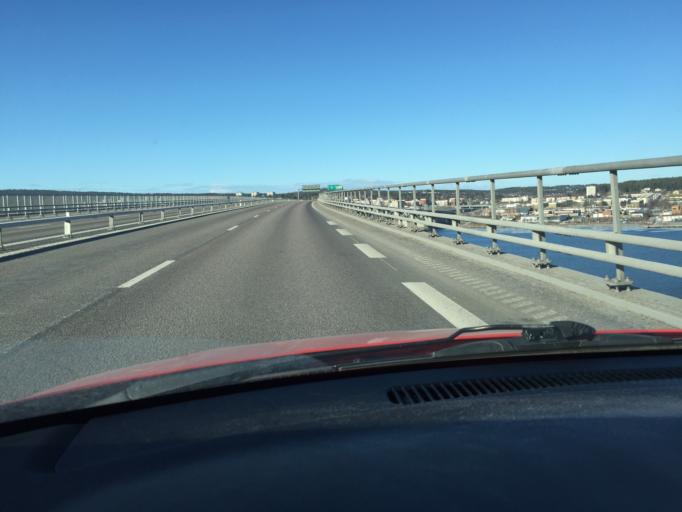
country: SE
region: Vaesternorrland
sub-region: Sundsvalls Kommun
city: Sundsvall
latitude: 62.3863
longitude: 17.3441
